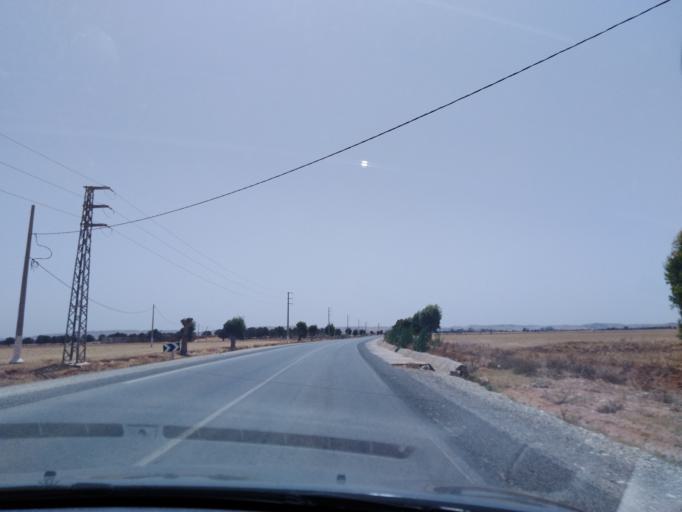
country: MA
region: Doukkala-Abda
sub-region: Safi
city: Safi
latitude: 32.2139
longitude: -8.9157
